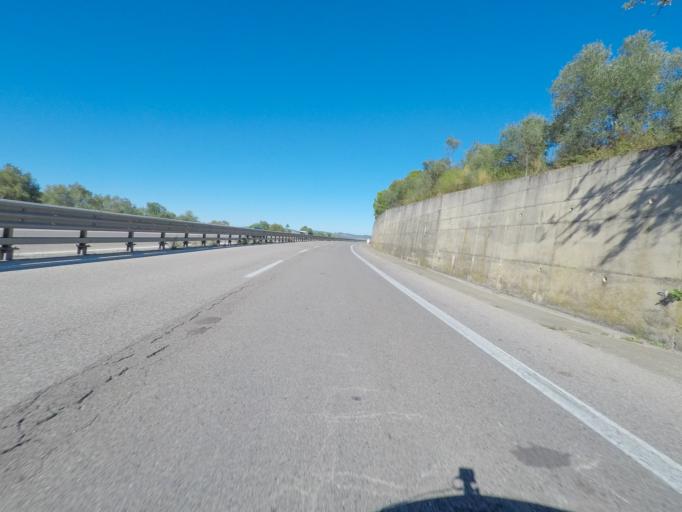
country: IT
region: Tuscany
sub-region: Provincia di Grosseto
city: Grosseto
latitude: 42.7377
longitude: 11.1377
